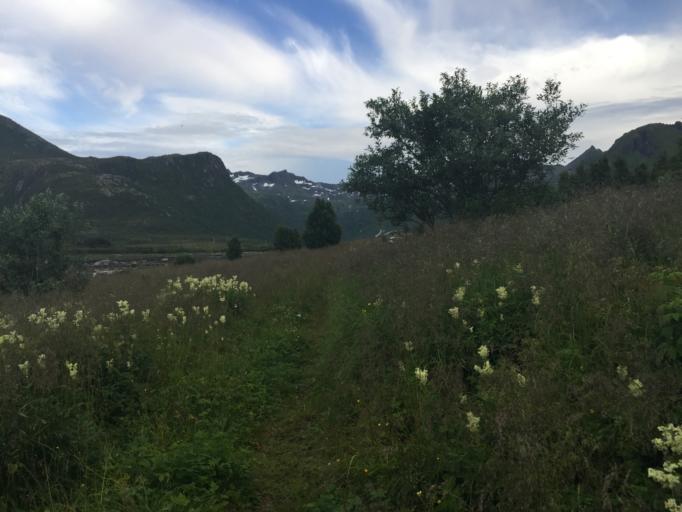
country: NO
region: Nordland
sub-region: Vagan
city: Kabelvag
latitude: 68.3260
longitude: 14.3987
